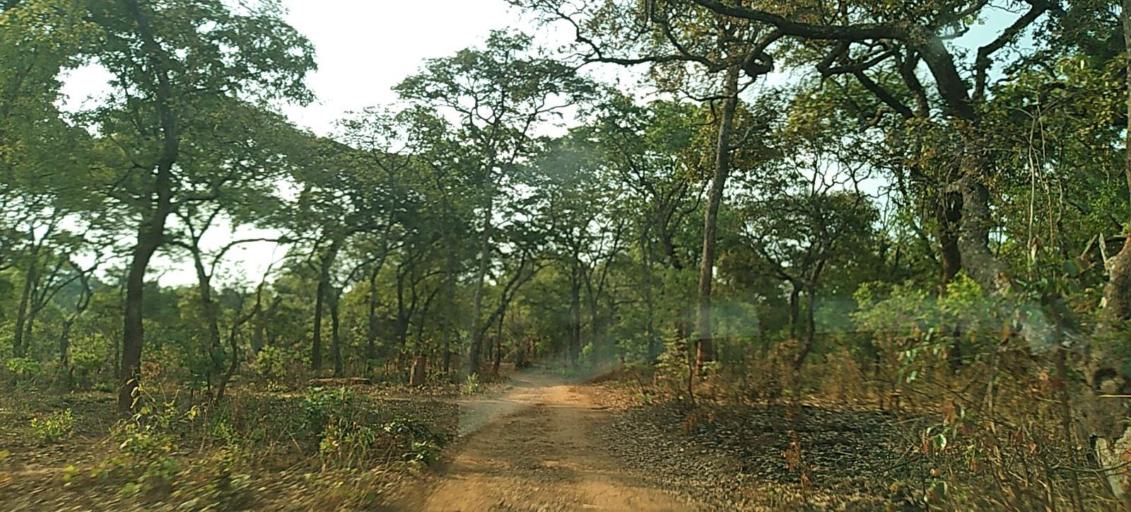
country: ZM
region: North-Western
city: Solwezi
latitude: -12.0626
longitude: 26.1738
